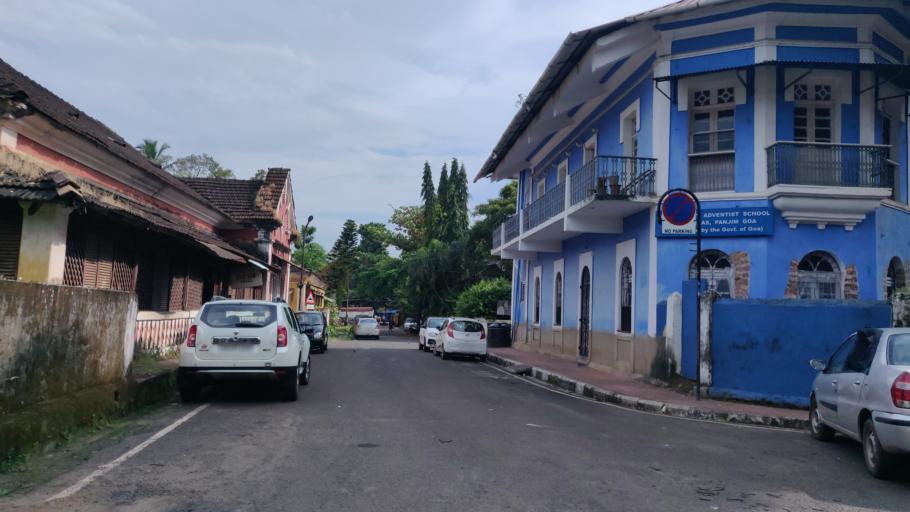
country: IN
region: Goa
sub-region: North Goa
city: Panaji
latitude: 15.4952
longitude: 73.8312
